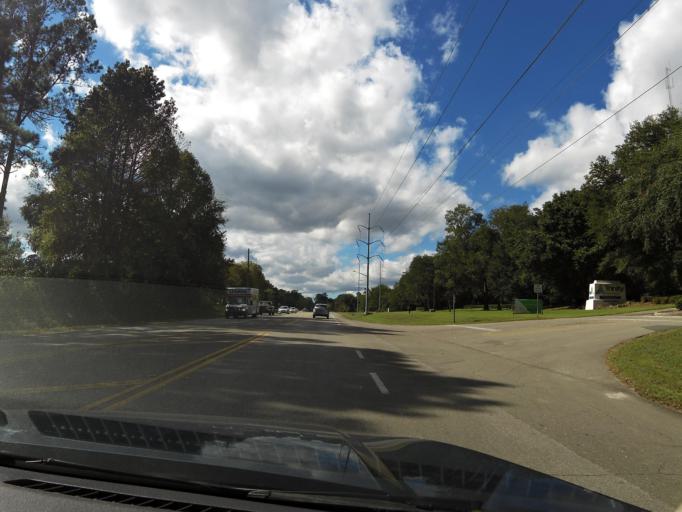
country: US
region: Florida
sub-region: Alachua County
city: Alachua
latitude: 29.7034
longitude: -82.3839
